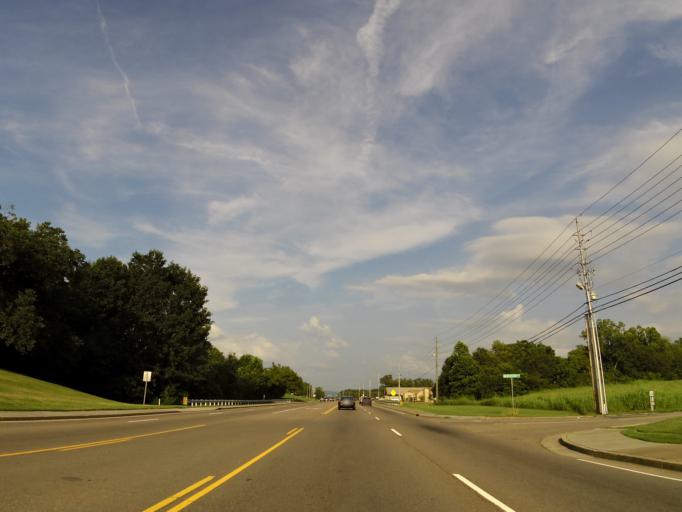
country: US
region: Tennessee
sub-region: Sevier County
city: Sevierville
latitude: 35.8638
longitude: -83.5369
